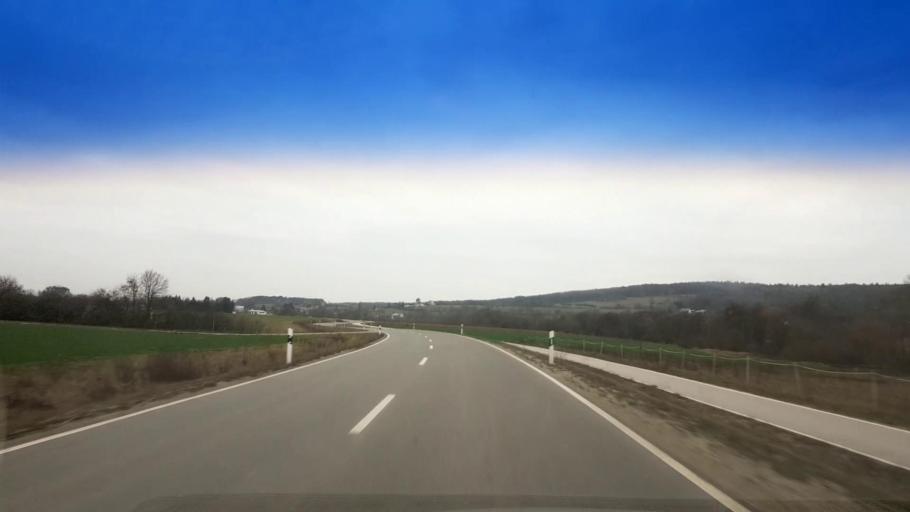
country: DE
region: Bavaria
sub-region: Upper Franconia
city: Pettstadt
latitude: 49.8032
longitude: 10.9435
